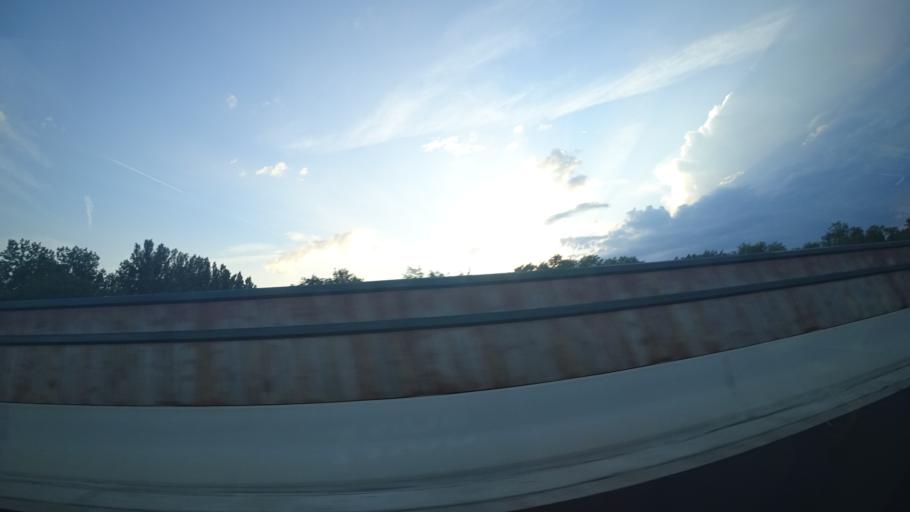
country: FR
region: Languedoc-Roussillon
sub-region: Departement de l'Herault
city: Pezenas
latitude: 43.4629
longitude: 3.4318
